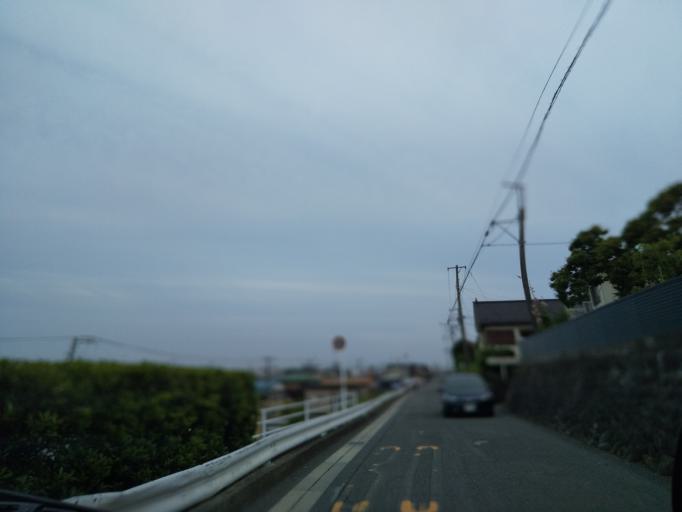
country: JP
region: Kanagawa
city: Atsugi
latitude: 35.4698
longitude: 139.3540
